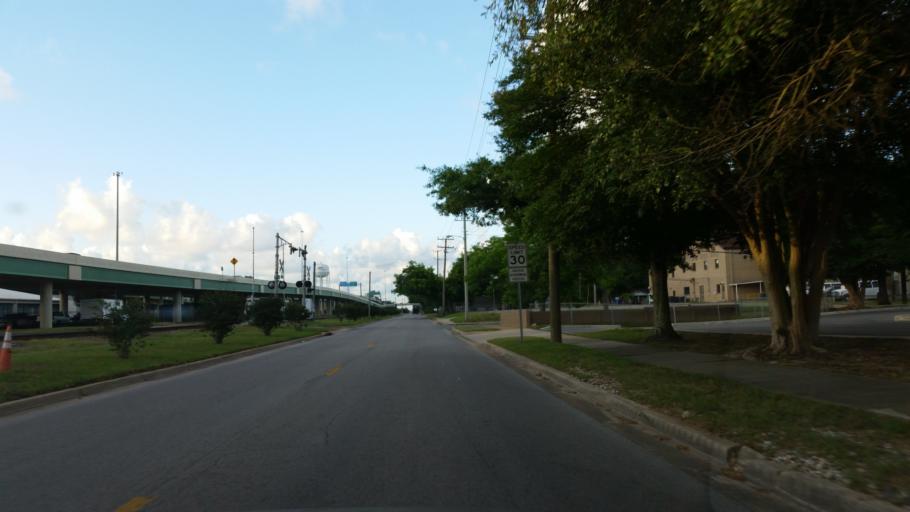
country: US
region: Florida
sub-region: Escambia County
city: Pensacola
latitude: 30.4281
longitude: -87.2162
